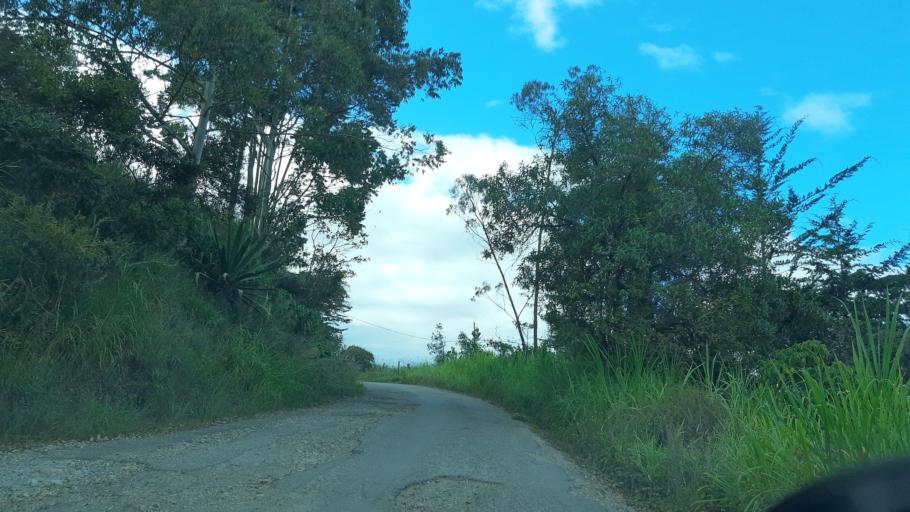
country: CO
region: Cundinamarca
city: Tenza
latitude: 5.0448
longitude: -73.4203
